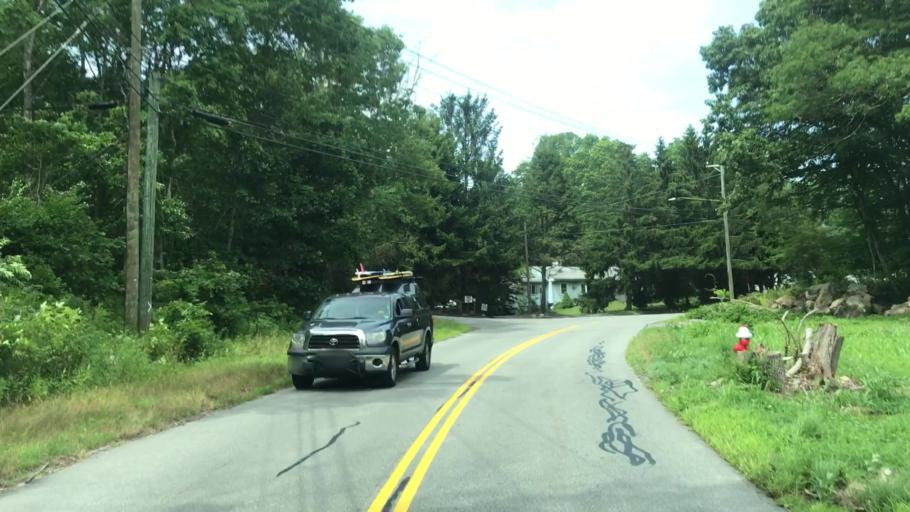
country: US
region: Connecticut
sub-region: New London County
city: Niantic
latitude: 41.3351
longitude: -72.2187
